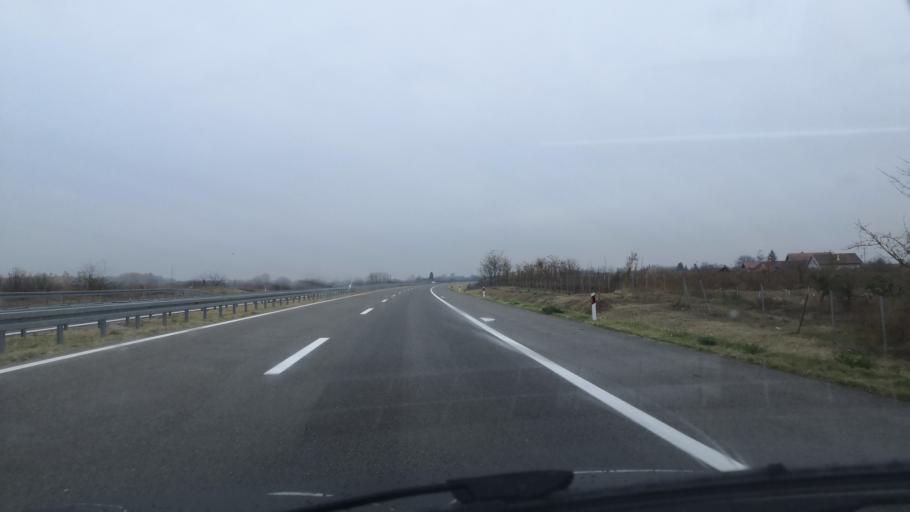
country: HU
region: Csongrad
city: Asotthalom
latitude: 46.1197
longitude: 19.8090
